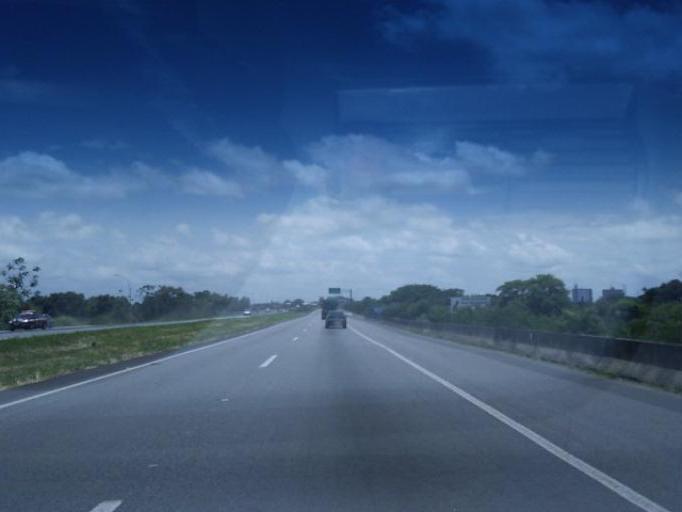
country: BR
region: Sao Paulo
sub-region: Registro
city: Registro
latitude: -24.4859
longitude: -47.8339
